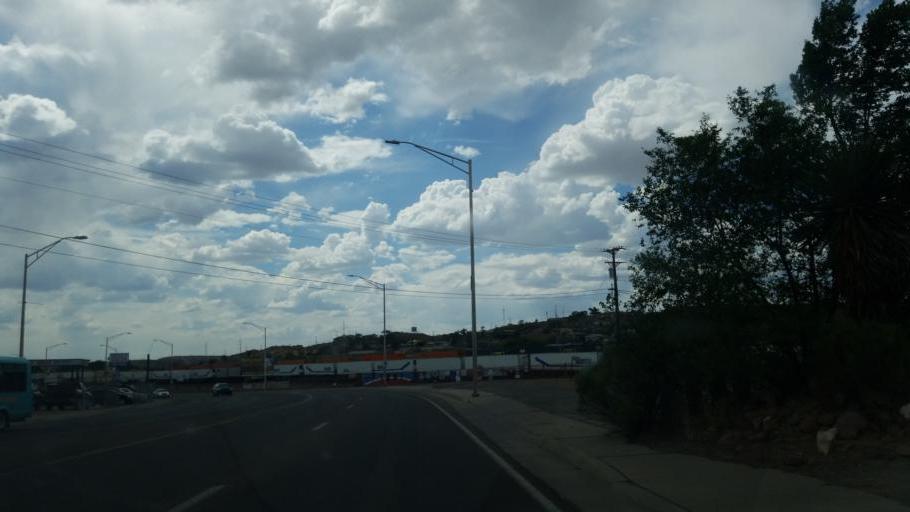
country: US
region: New Mexico
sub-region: McKinley County
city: Gallup
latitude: 35.5306
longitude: -108.7320
